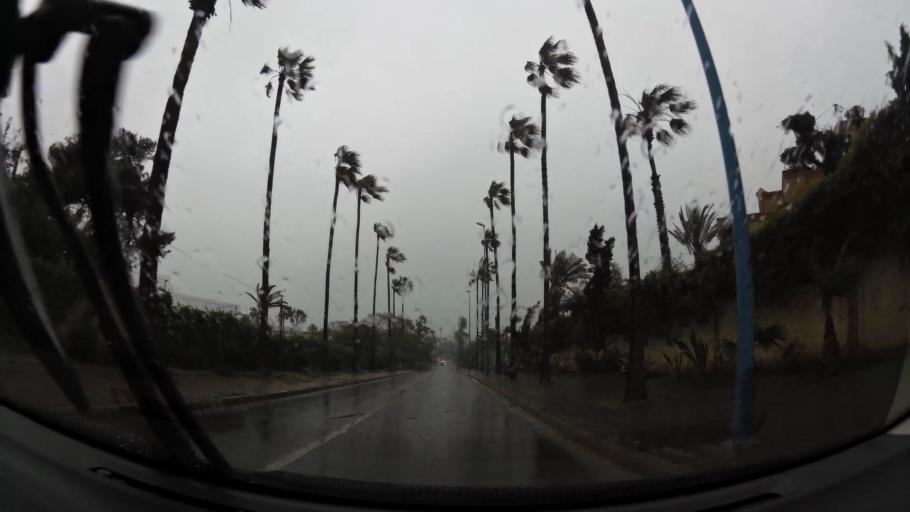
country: MA
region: Grand Casablanca
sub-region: Casablanca
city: Casablanca
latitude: 33.5887
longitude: -7.6673
